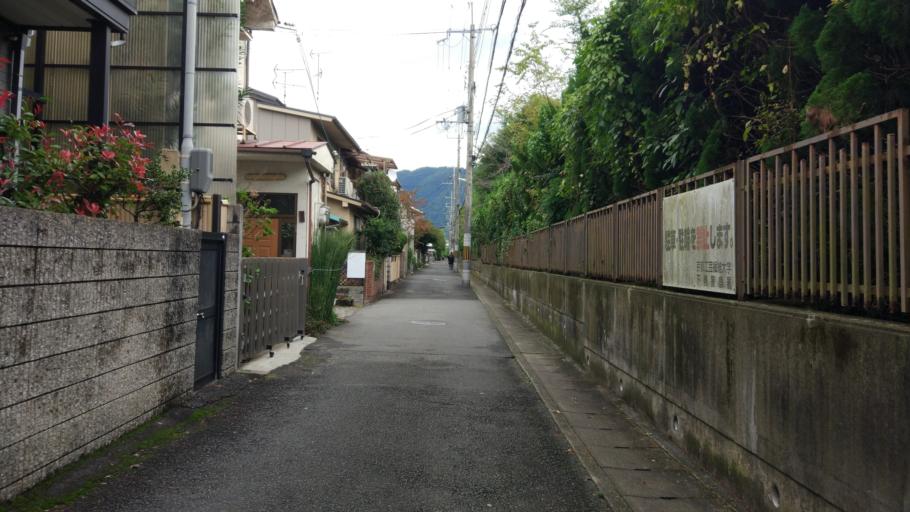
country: JP
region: Kyoto
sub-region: Kyoto-shi
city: Kamigyo-ku
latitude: 35.0507
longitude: 135.7792
